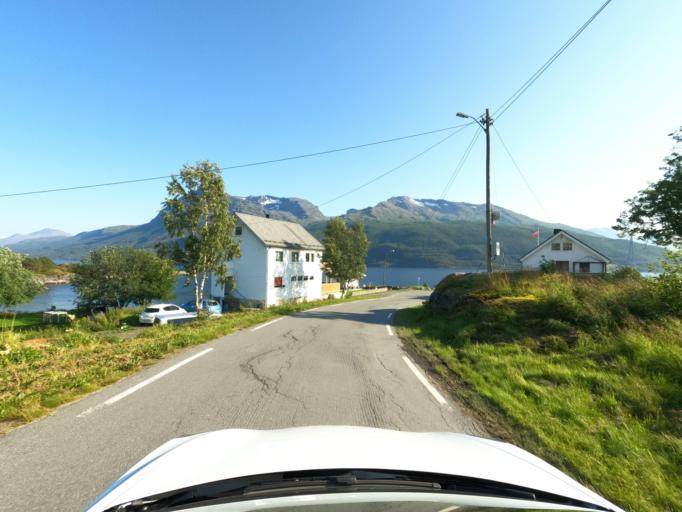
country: NO
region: Nordland
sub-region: Narvik
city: Narvik
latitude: 68.4707
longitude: 17.5042
